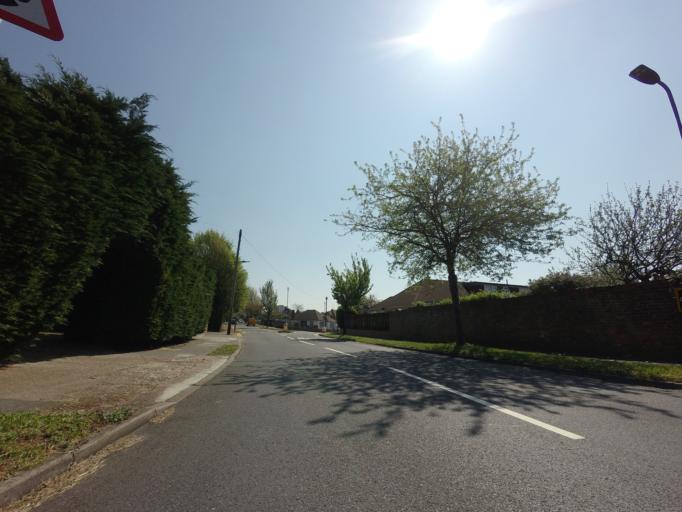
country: GB
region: England
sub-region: Greater London
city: Orpington
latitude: 51.3811
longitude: 0.1097
